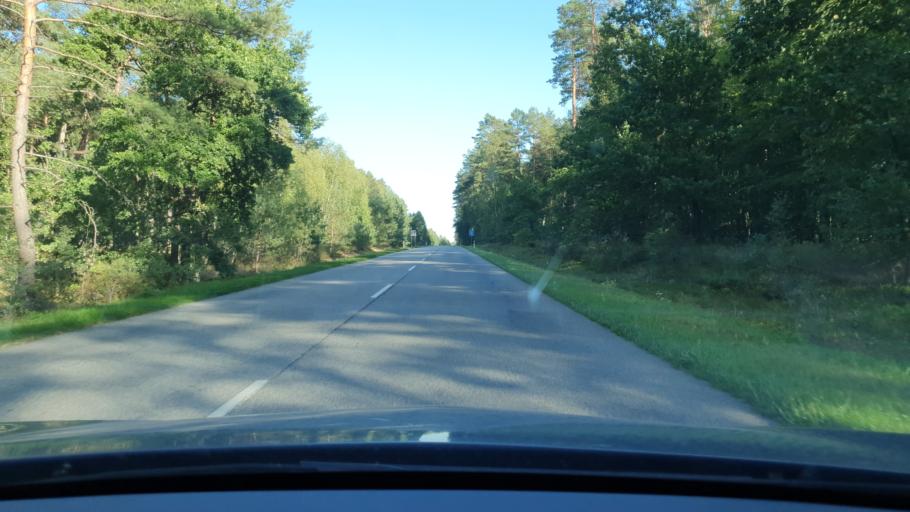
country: PL
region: West Pomeranian Voivodeship
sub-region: Powiat kamienski
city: Golczewo
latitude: 53.8127
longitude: 15.0947
